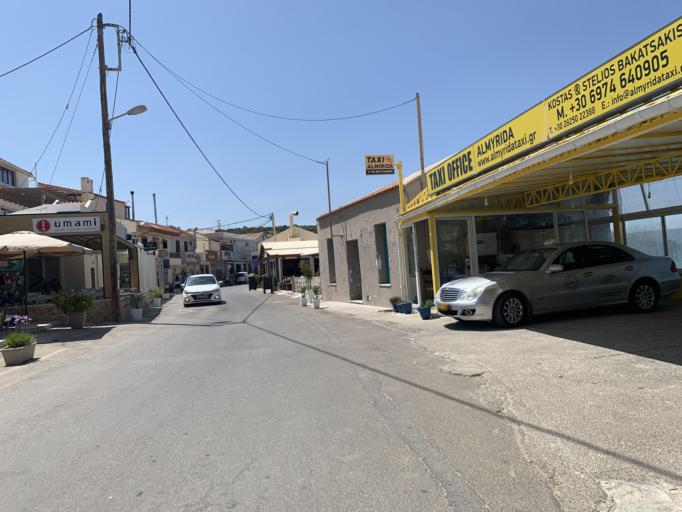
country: GR
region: Crete
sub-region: Nomos Chanias
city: Kalivai
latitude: 35.4492
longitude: 24.1998
